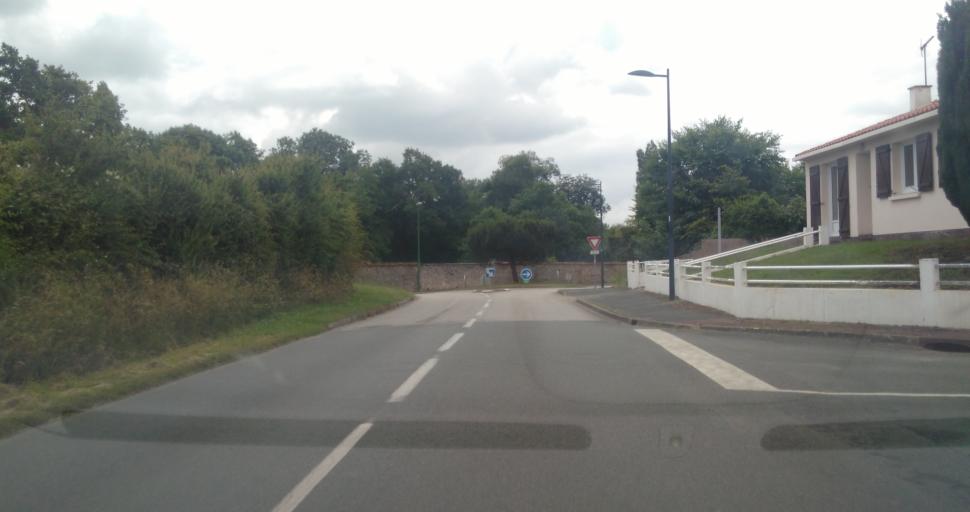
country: FR
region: Pays de la Loire
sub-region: Departement de la Vendee
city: La Chaize-le-Vicomte
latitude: 46.6762
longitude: -1.2952
